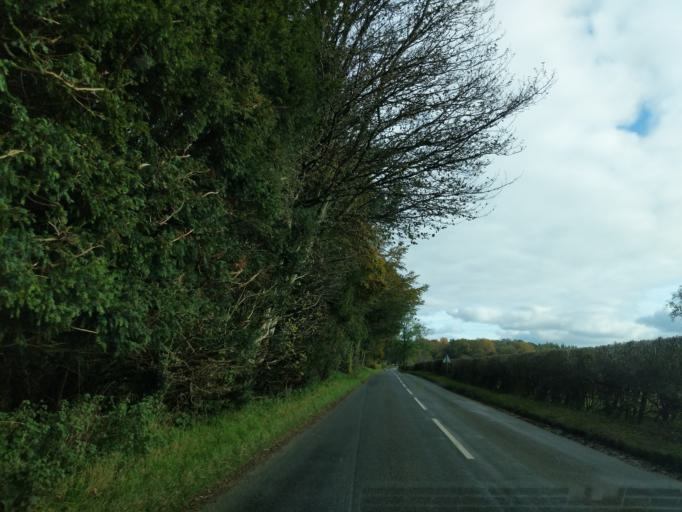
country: GB
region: Scotland
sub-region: Dumfries and Galloway
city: Thornhill
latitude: 55.2405
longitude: -3.7861
